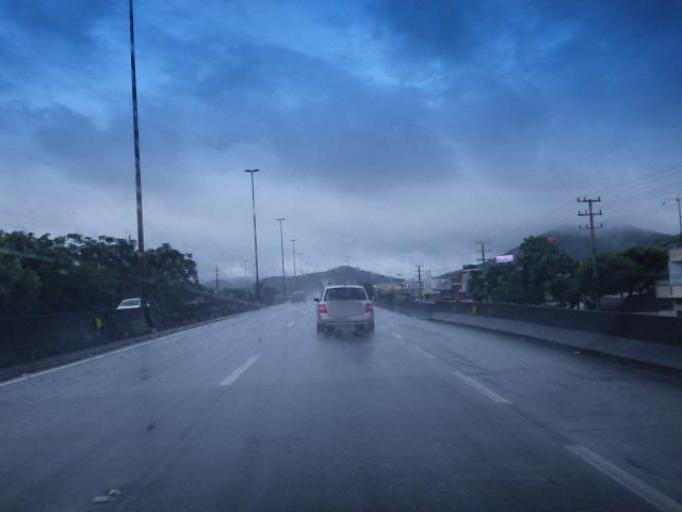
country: BR
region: Santa Catarina
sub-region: Balneario Camboriu
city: Balneario Camboriu
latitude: -27.0020
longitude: -48.6366
